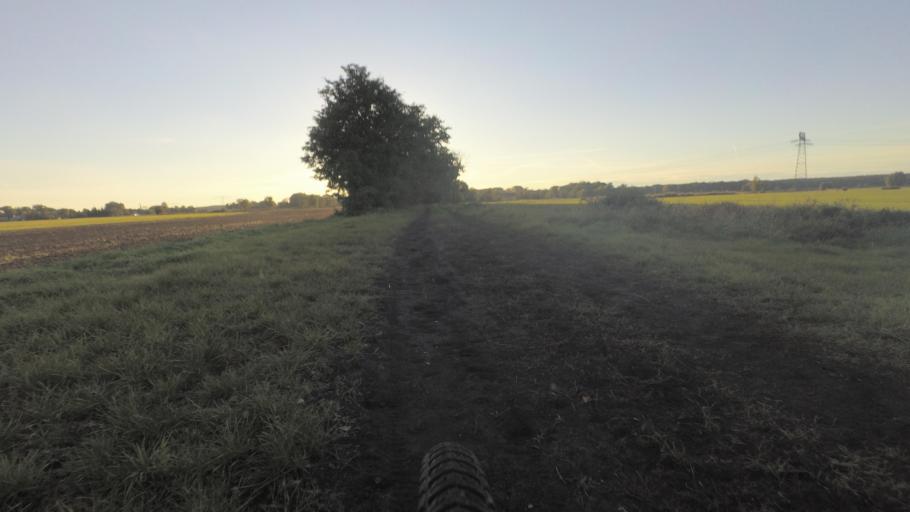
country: DE
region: Brandenburg
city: Ludwigsfelde
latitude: 52.2726
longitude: 13.3186
